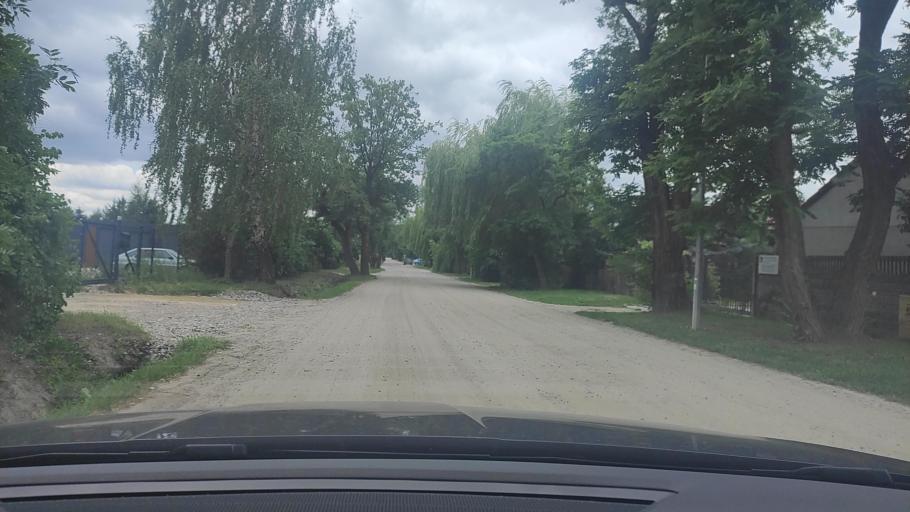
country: PL
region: Greater Poland Voivodeship
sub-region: Powiat poznanski
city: Swarzedz
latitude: 52.3856
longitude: 17.1166
